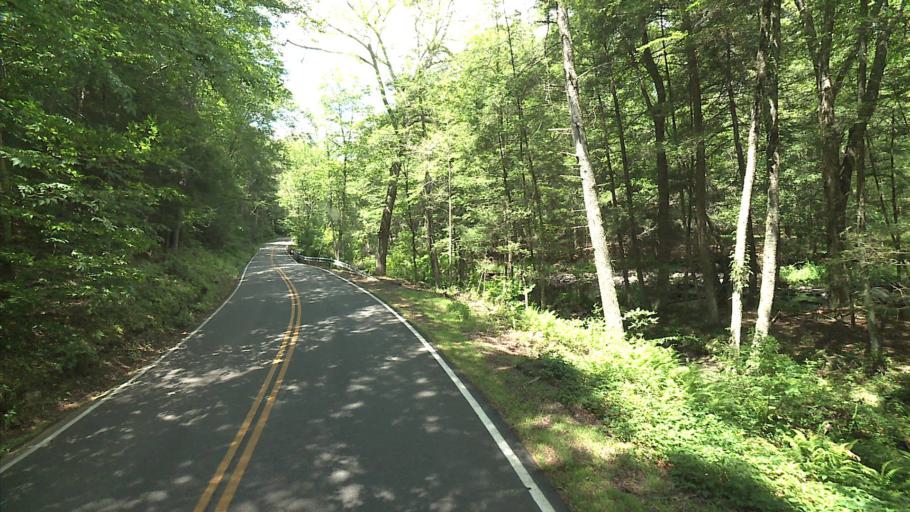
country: US
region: Connecticut
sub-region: New London County
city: Colchester
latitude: 41.4629
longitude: -72.3369
